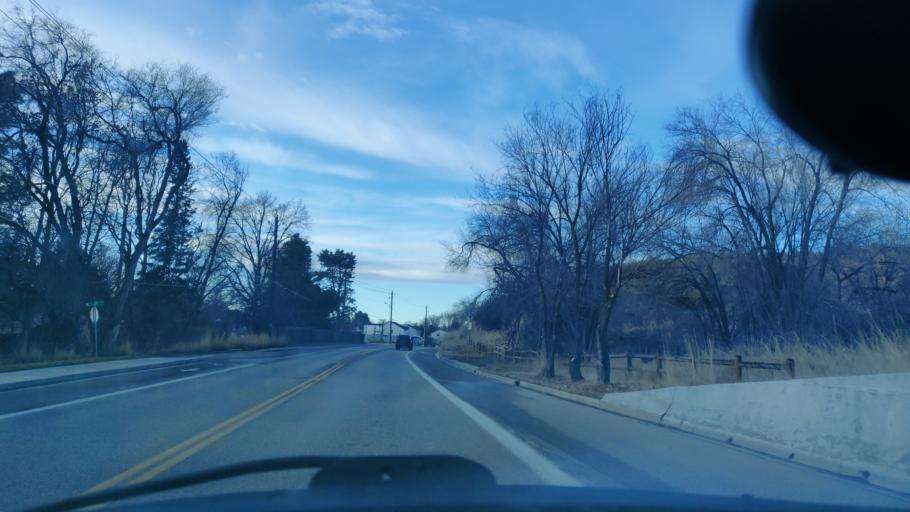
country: US
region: Idaho
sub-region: Ada County
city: Garden City
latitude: 43.6514
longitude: -116.2270
